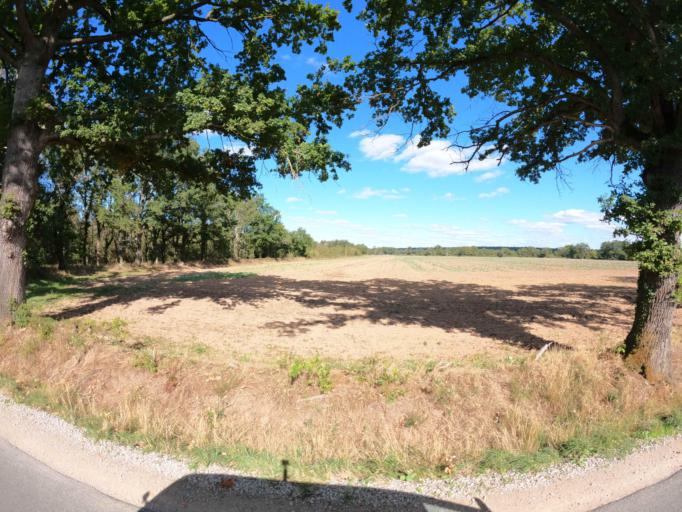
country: FR
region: Auvergne
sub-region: Departement de l'Allier
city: Doyet
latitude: 46.3940
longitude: 2.7545
